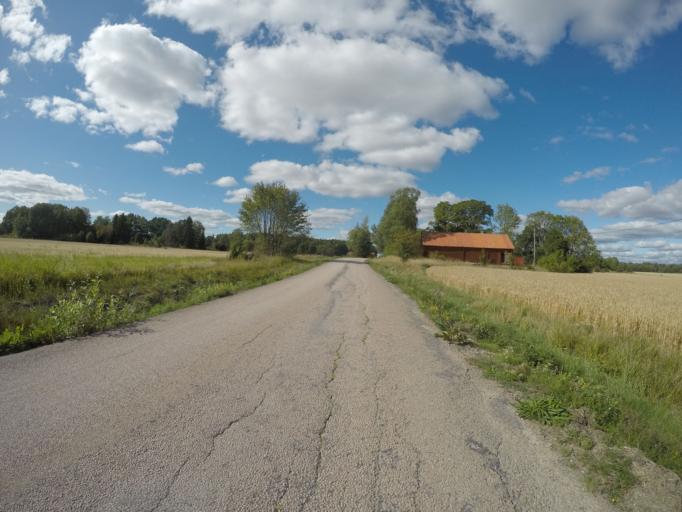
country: SE
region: Vaestmanland
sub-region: Hallstahammars Kommun
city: Kolback
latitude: 59.5113
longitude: 16.1887
